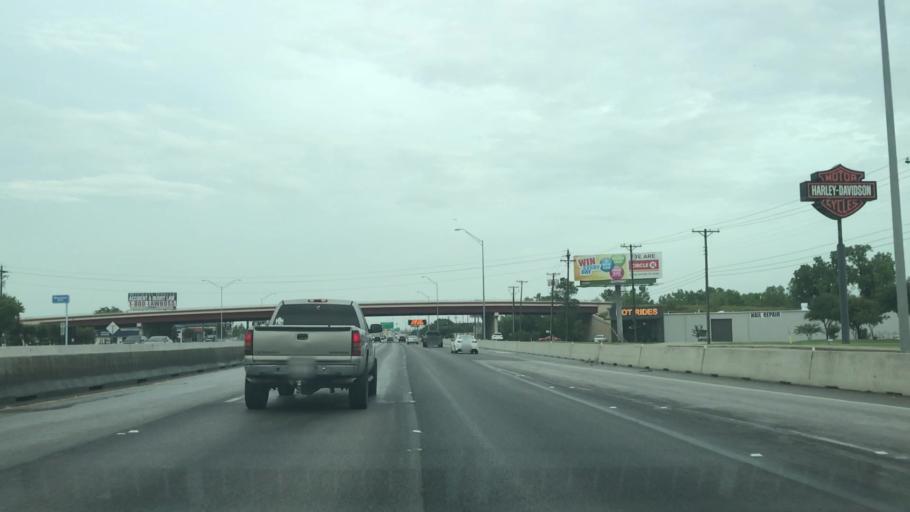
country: US
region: Texas
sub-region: Dallas County
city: Carrollton
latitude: 32.9660
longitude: -96.9184
